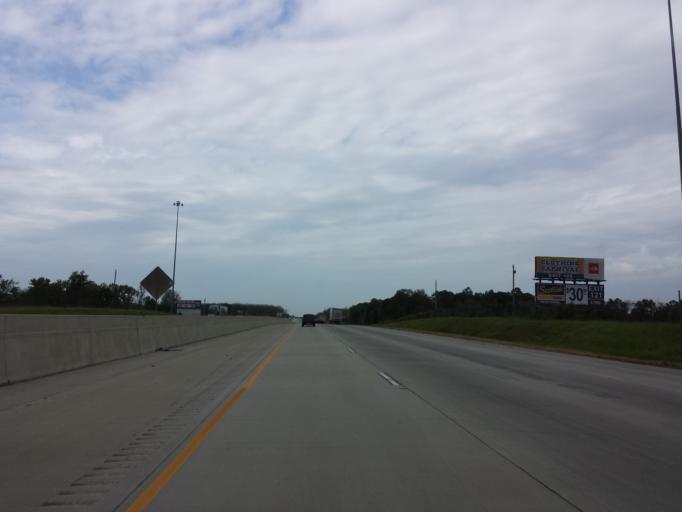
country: US
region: Georgia
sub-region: Crisp County
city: Cordele
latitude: 32.0112
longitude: -83.7595
